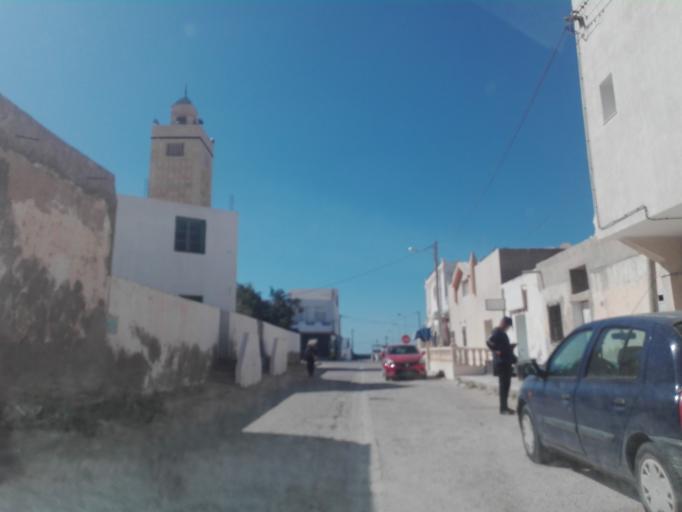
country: TN
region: Safaqis
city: Al Qarmadah
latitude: 34.7055
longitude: 11.2016
